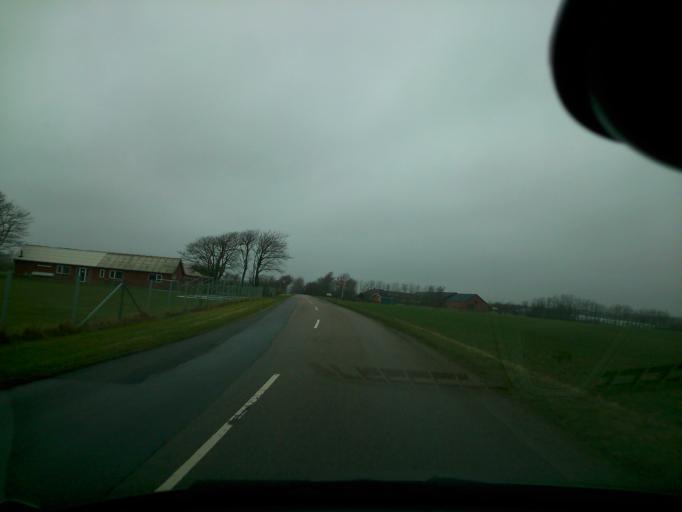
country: DK
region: Central Jutland
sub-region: Ringkobing-Skjern Kommune
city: Ringkobing
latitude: 56.1031
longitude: 8.4158
